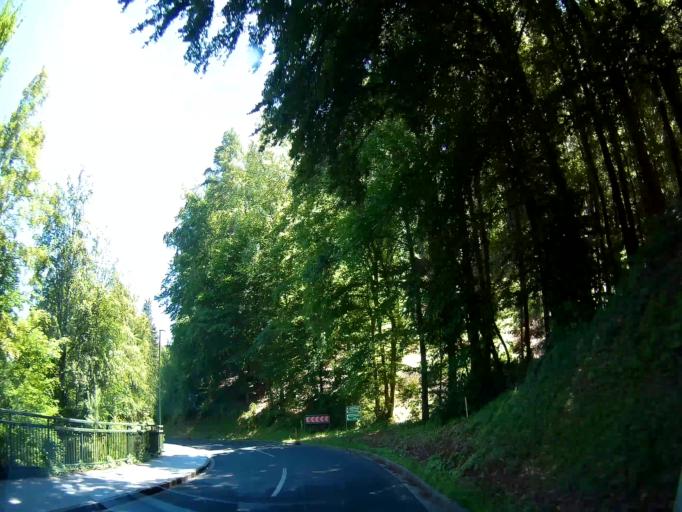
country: AT
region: Carinthia
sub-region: Politischer Bezirk Klagenfurt Land
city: Maria Worth
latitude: 46.6119
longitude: 14.1742
